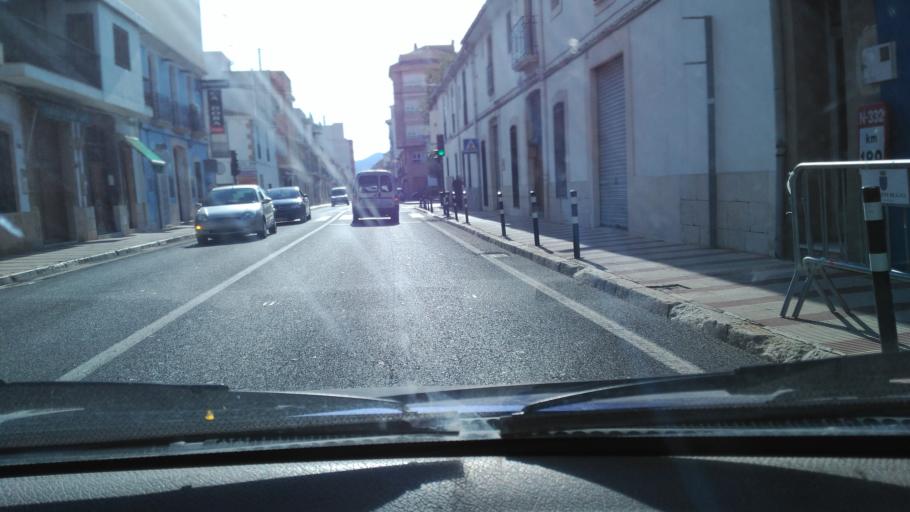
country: ES
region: Valencia
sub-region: Provincia de Alicante
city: Gata de Gorgos
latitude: 38.7740
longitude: 0.0868
